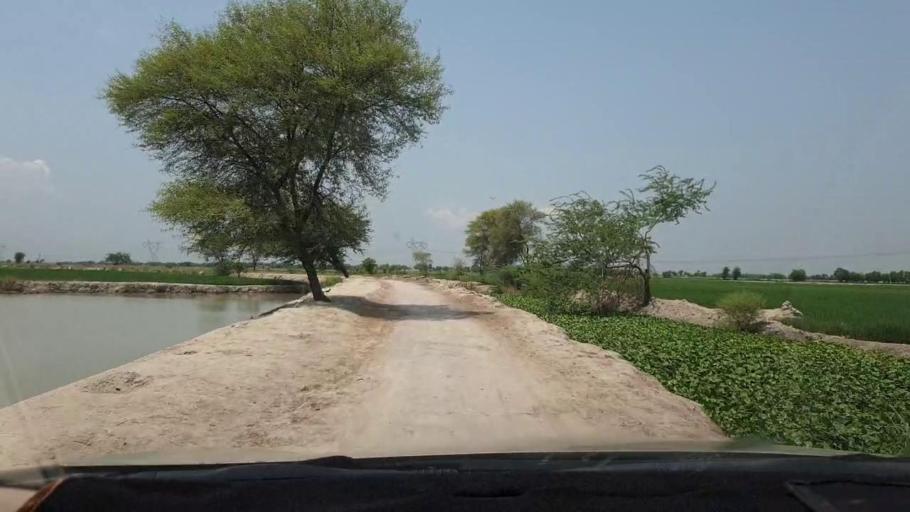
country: PK
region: Sindh
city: Naudero
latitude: 27.6719
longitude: 68.2970
